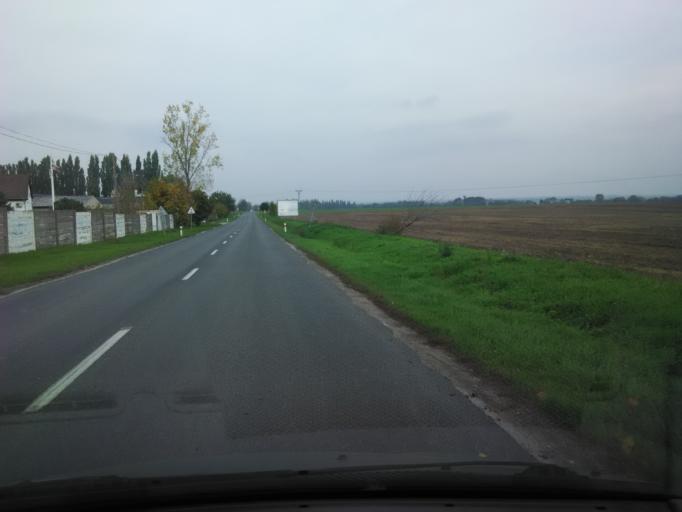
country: SK
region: Nitriansky
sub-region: Okres Nove Zamky
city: Nove Zamky
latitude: 47.9681
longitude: 18.2543
